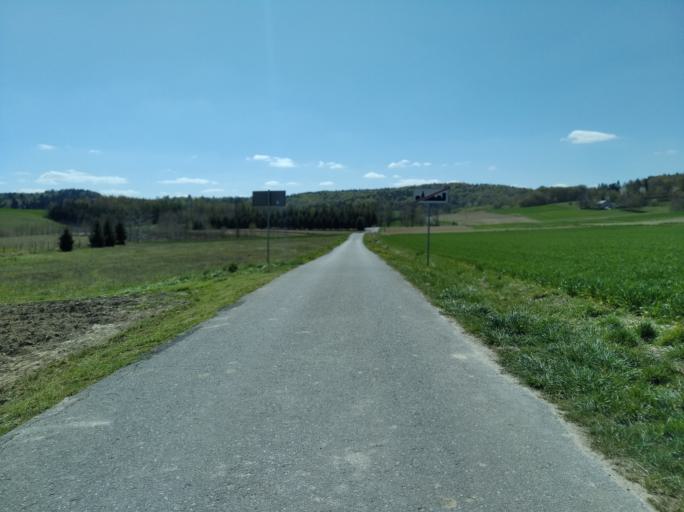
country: PL
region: Subcarpathian Voivodeship
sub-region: Powiat strzyzowski
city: Wisniowa
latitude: 49.9081
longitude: 21.6810
